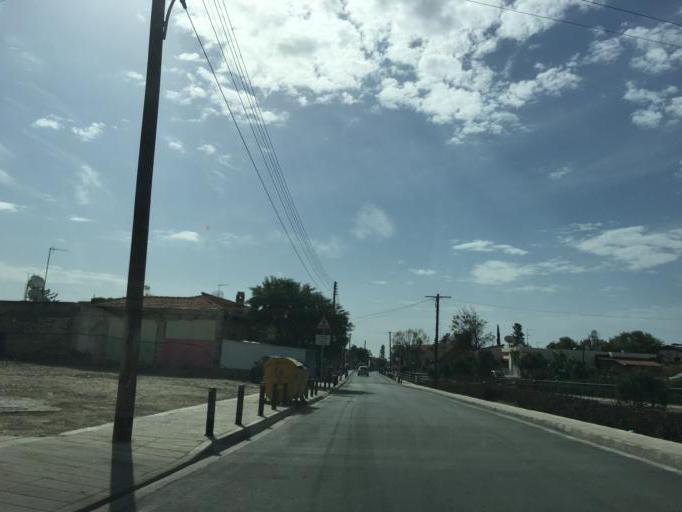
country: CY
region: Limassol
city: Limassol
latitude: 34.6740
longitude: 33.0363
